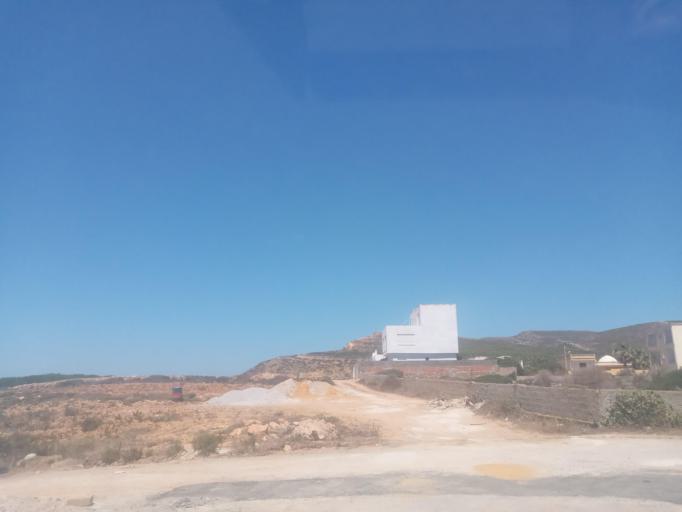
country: TN
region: Nabul
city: El Haouaria
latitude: 37.0566
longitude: 11.0037
